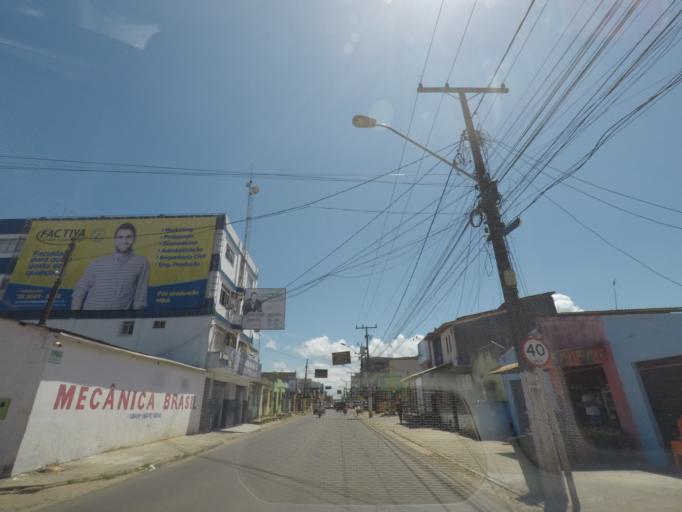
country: BR
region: Bahia
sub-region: Valenca
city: Valenca
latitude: -13.3631
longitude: -39.0685
